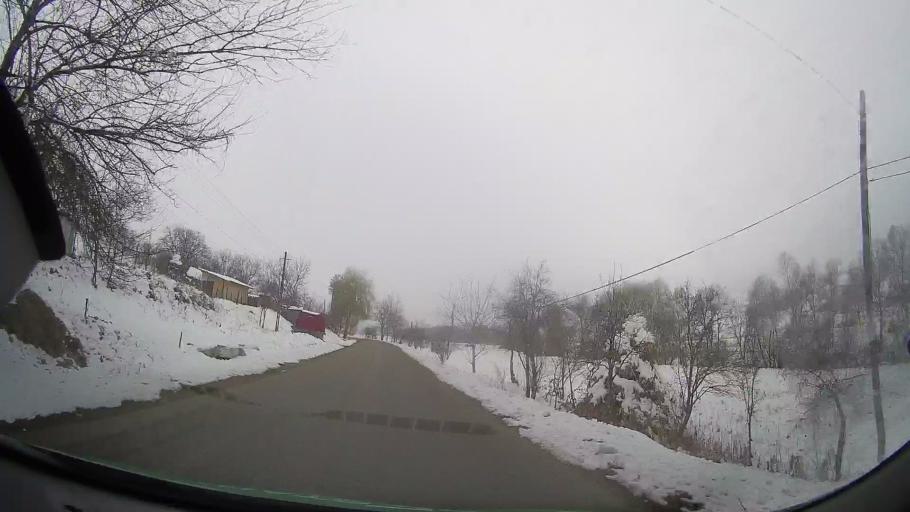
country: RO
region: Bacau
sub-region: Comuna Vultureni
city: Vultureni
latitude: 46.3828
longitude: 27.2765
